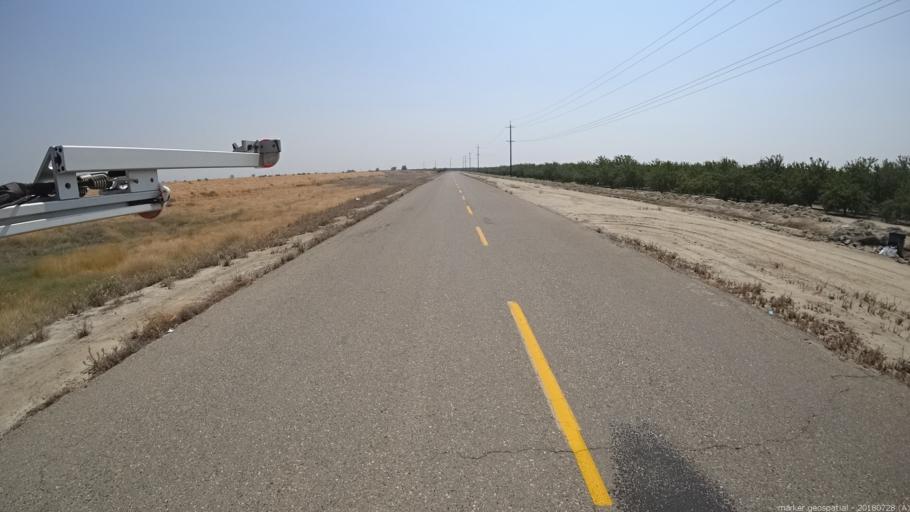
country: US
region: California
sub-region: Fresno County
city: Mendota
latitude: 36.8100
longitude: -120.3081
